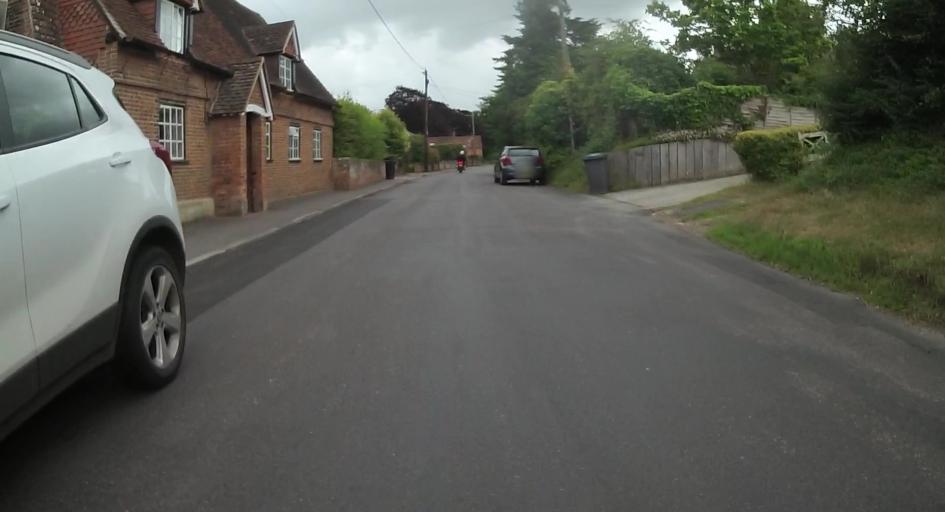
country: GB
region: England
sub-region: Hampshire
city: Fleet
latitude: 51.2300
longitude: -0.8573
